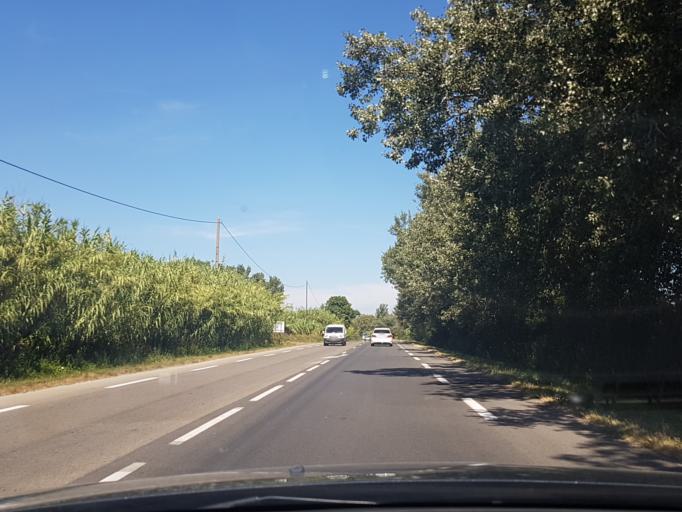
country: FR
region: Provence-Alpes-Cote d'Azur
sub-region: Departement des Bouches-du-Rhone
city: Eyragues
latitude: 43.8194
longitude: 4.8363
